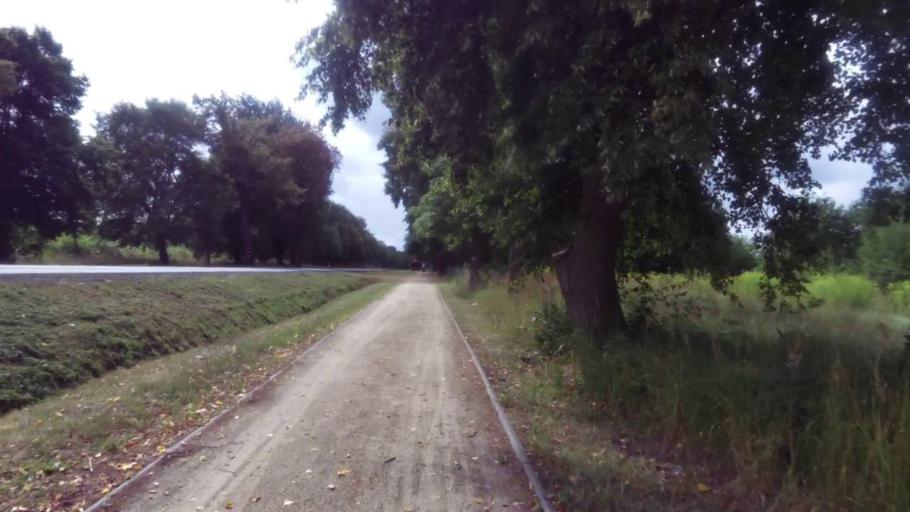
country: PL
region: West Pomeranian Voivodeship
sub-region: Powiat mysliborski
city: Debno
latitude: 52.7271
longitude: 14.6937
